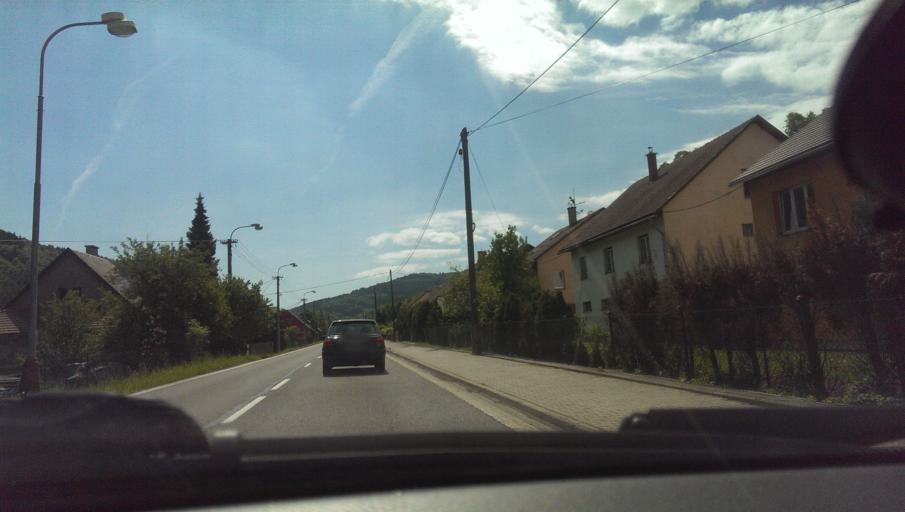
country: CZ
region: Zlin
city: Valasska Polanka
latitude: 49.2532
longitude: 17.9981
